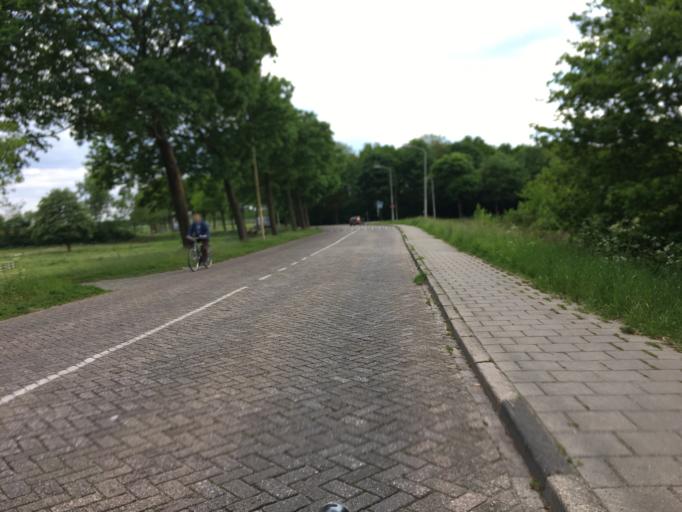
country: NL
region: Gelderland
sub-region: Gemeente Maasdriel
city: Hedel
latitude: 51.6912
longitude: 5.2193
